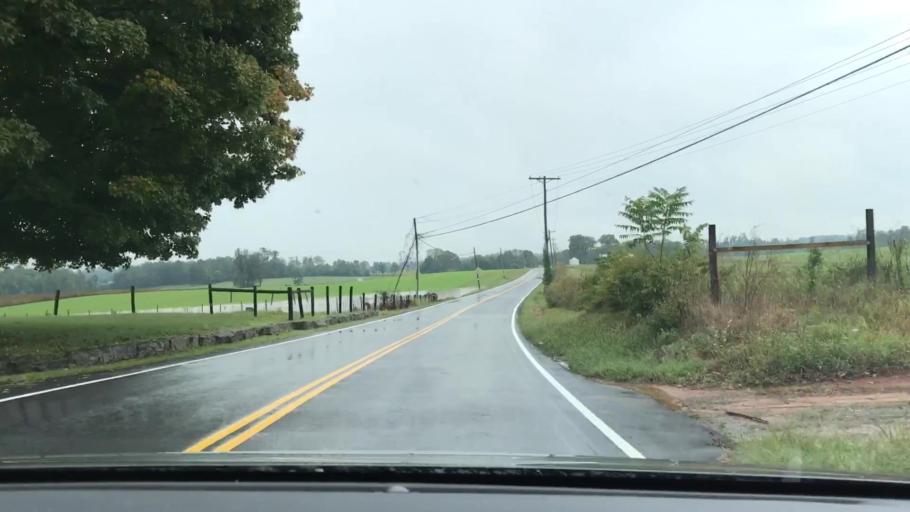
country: US
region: Tennessee
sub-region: Macon County
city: Red Boiling Springs
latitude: 36.4553
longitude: -85.8807
